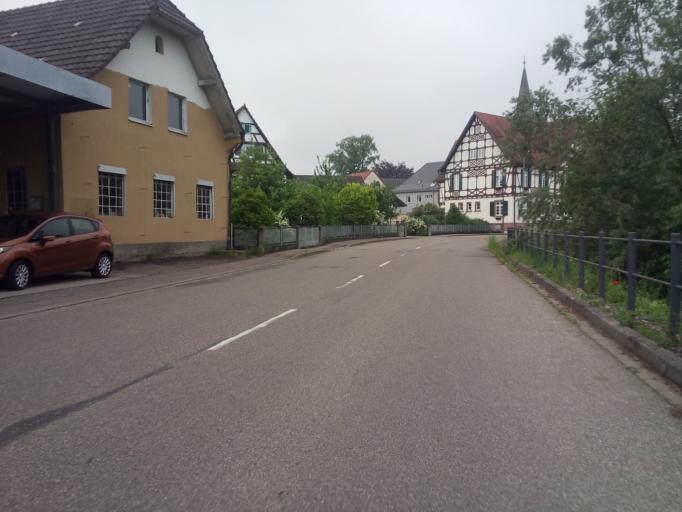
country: DE
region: Baden-Wuerttemberg
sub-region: Freiburg Region
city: Rheinau
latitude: 48.6685
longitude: 7.9353
